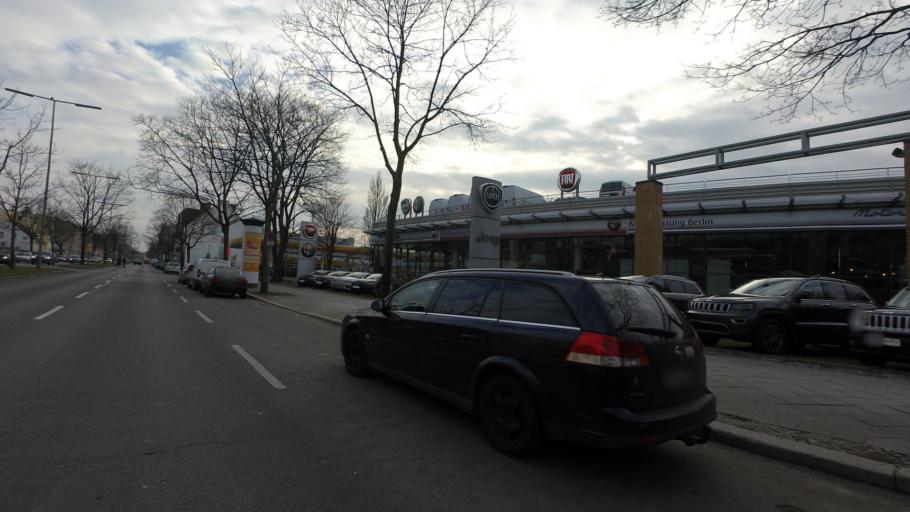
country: DE
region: Berlin
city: Reinickendorf
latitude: 52.5717
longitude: 13.3307
